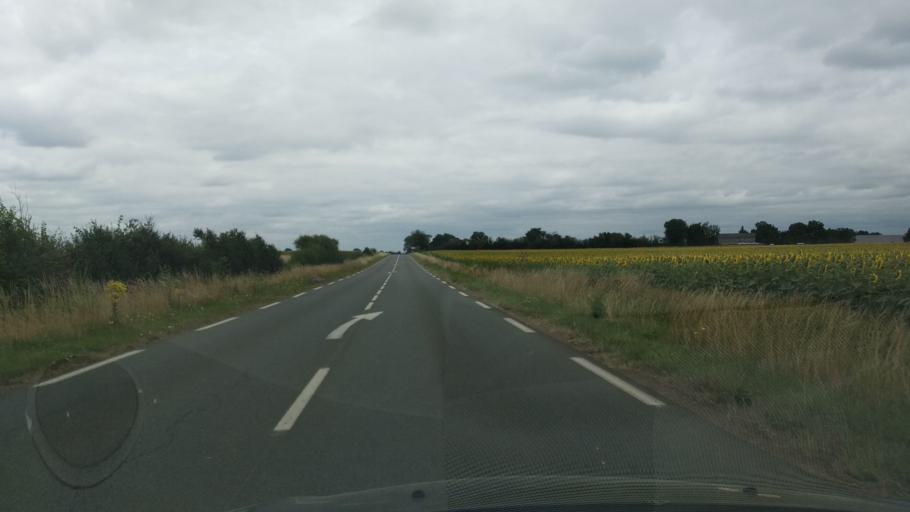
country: FR
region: Poitou-Charentes
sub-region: Departement de la Vienne
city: La Villedieu-du-Clain
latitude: 46.4299
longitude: 0.3767
